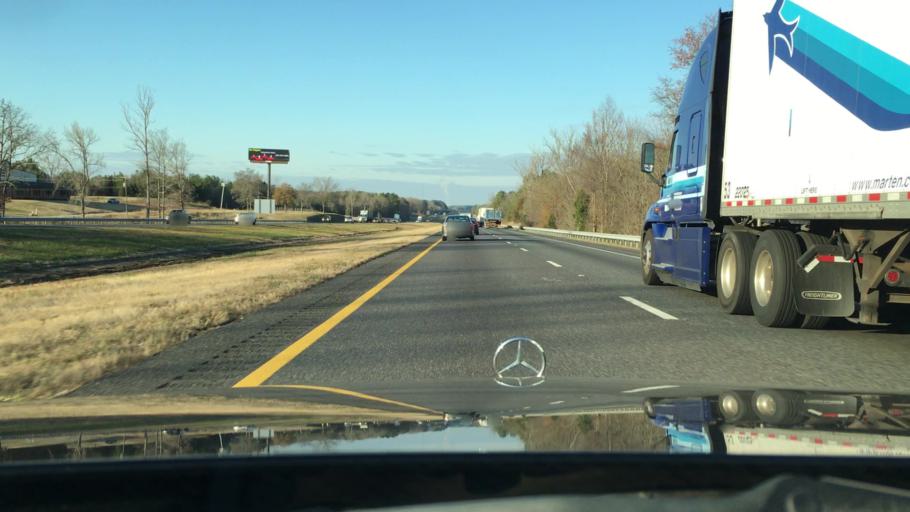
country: US
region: South Carolina
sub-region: York County
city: Lesslie
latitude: 34.7536
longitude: -81.0360
